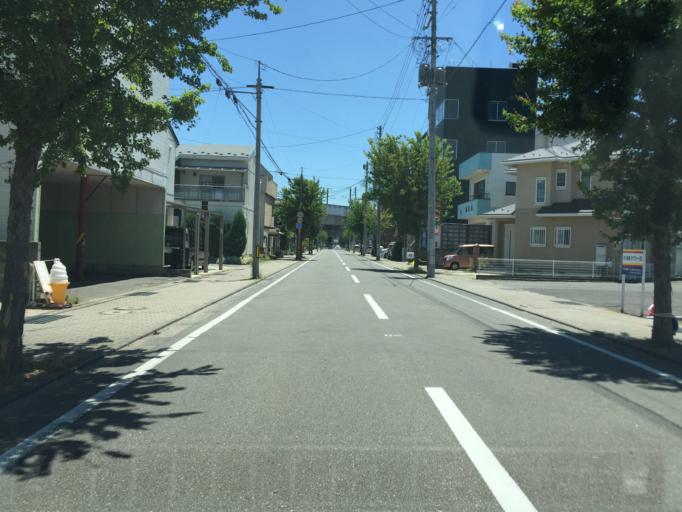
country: JP
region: Fukushima
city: Fukushima-shi
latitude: 37.7649
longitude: 140.4569
